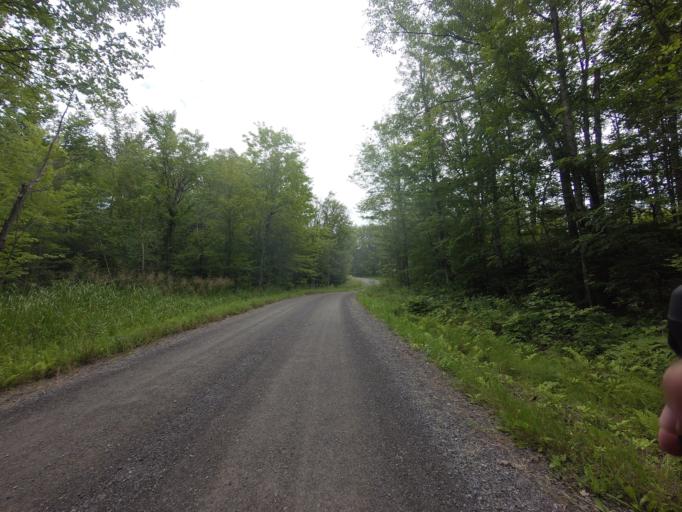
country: CA
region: Ontario
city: Perth
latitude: 44.7021
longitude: -76.6353
